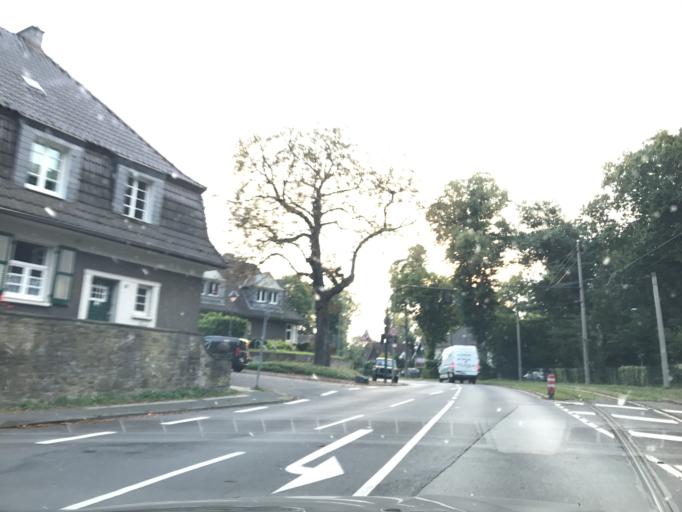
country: DE
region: North Rhine-Westphalia
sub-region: Regierungsbezirk Dusseldorf
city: Essen
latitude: 51.4347
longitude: 6.9785
